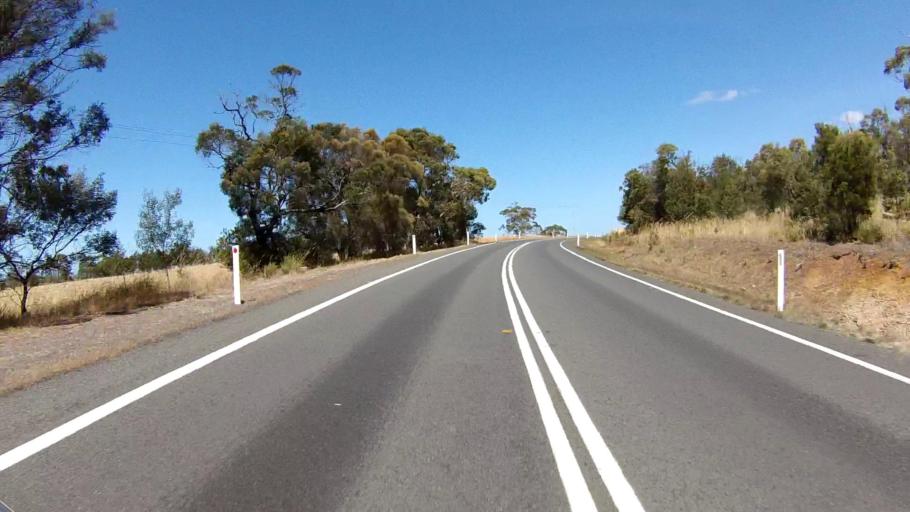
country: AU
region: Tasmania
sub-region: Break O'Day
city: St Helens
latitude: -42.0785
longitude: 148.0689
